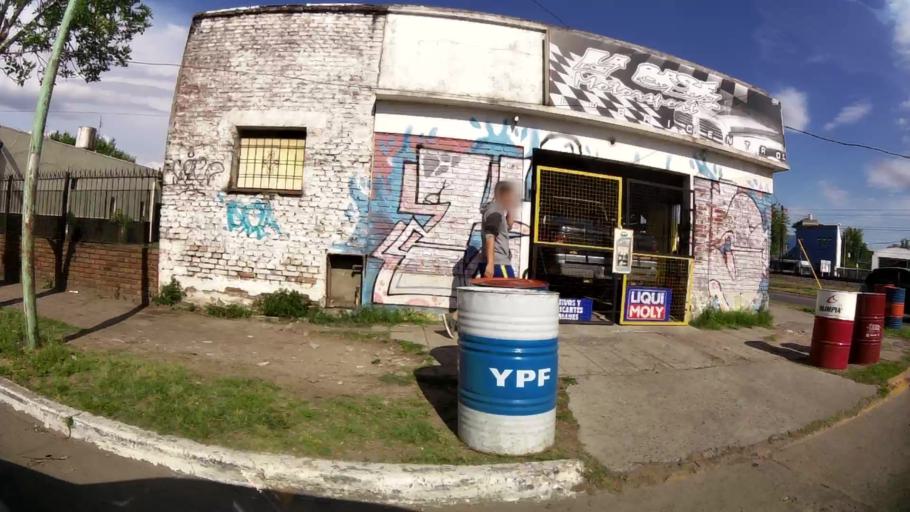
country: AR
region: Buenos Aires
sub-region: Partido de Merlo
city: Merlo
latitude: -34.6632
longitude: -58.7349
